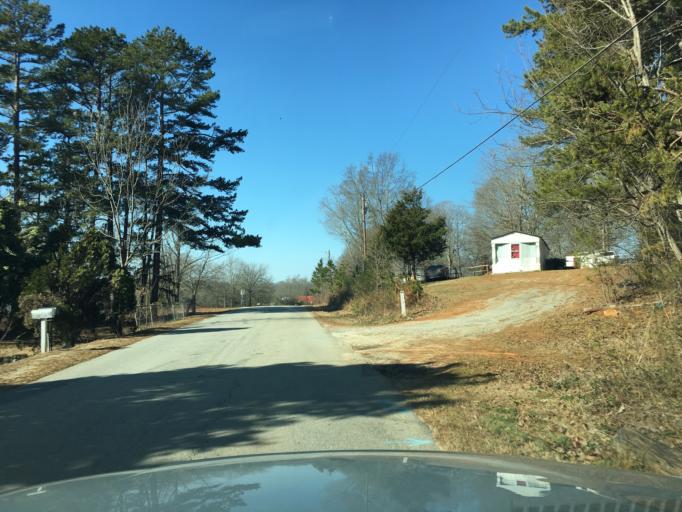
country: US
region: South Carolina
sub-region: Pickens County
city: Arial
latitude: 34.8734
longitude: -82.6593
